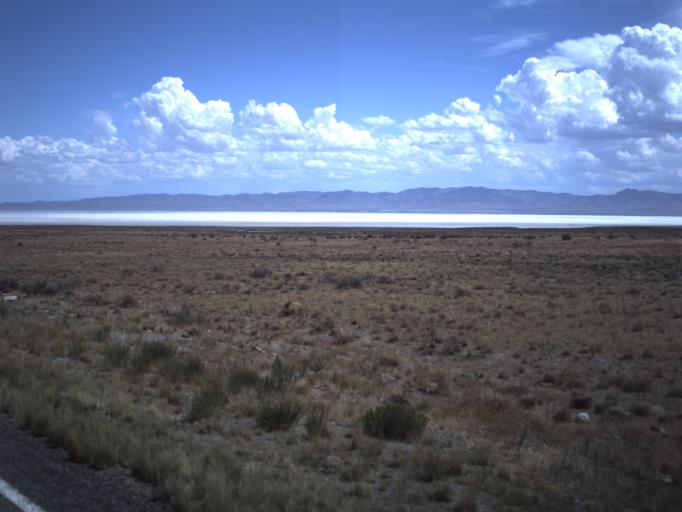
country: US
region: Utah
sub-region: Beaver County
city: Milford
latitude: 39.0545
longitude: -113.2613
